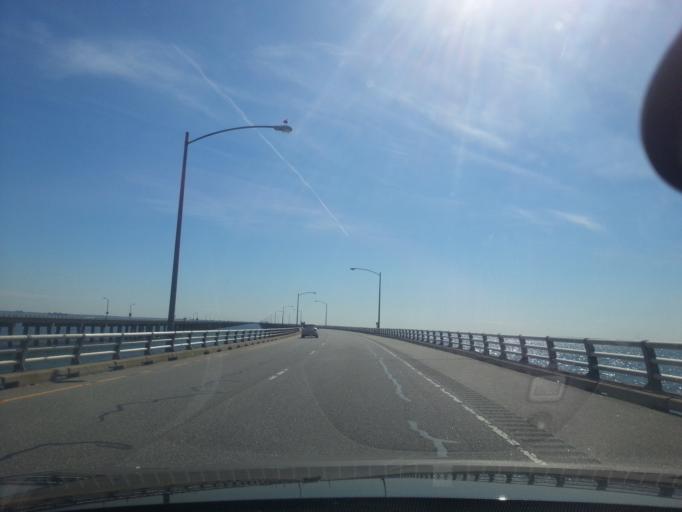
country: US
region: Virginia
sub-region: City of Virginia Beach
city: Virginia Beach
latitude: 37.0292
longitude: -76.0873
